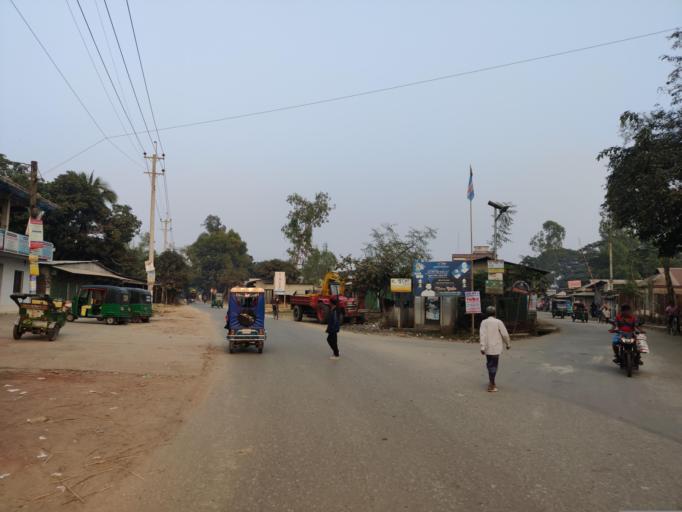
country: BD
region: Dhaka
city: Bajitpur
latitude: 24.1586
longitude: 90.8073
